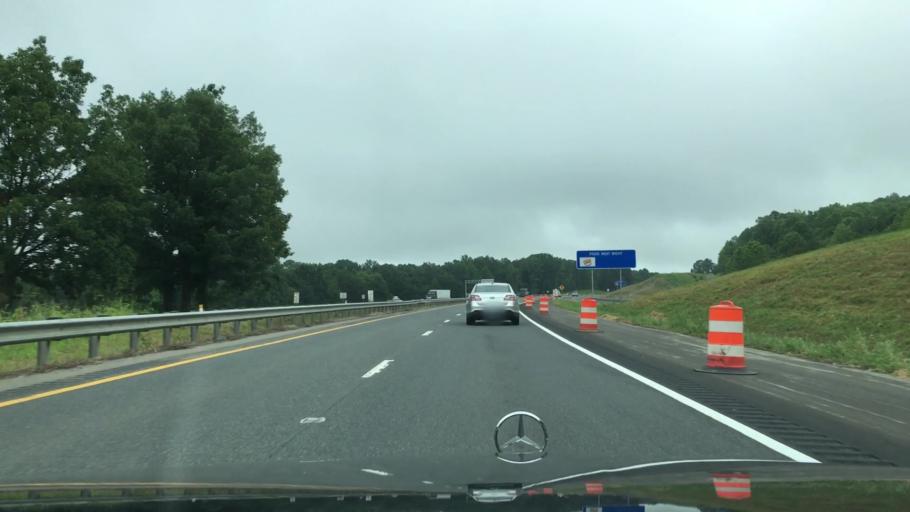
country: US
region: Virginia
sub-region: City of Lynchburg
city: Lynchburg
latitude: 37.3726
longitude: -79.1464
